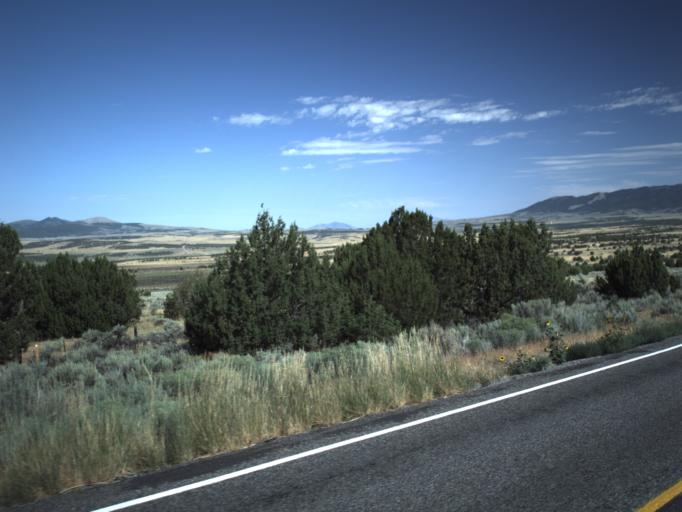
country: US
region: Utah
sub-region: Juab County
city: Mona
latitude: 39.8432
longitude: -112.1381
